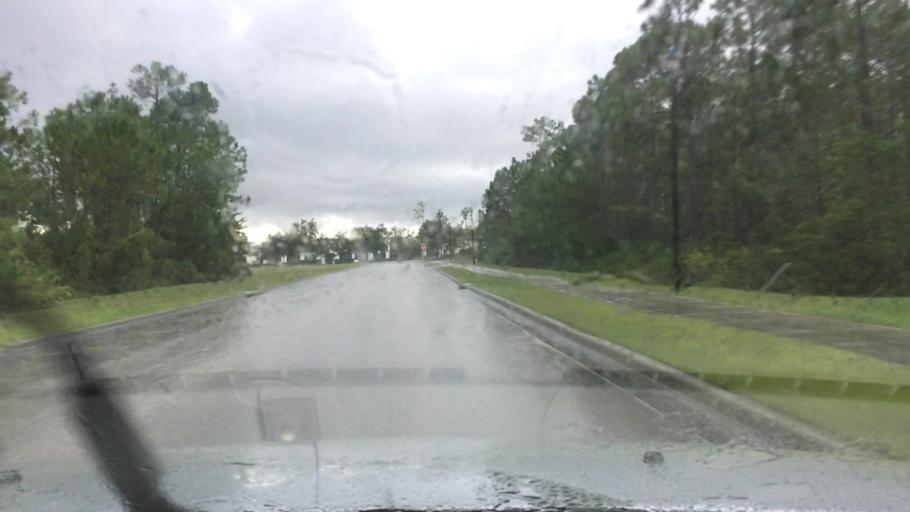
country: US
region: Florida
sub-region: Volusia County
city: Holly Hill
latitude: 29.2129
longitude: -81.0885
